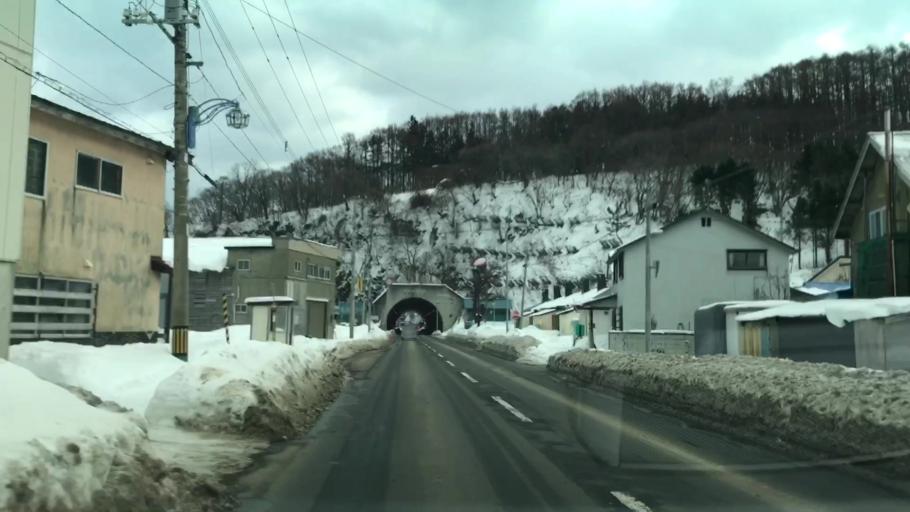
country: JP
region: Hokkaido
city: Yoichi
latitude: 43.2612
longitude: 140.6495
